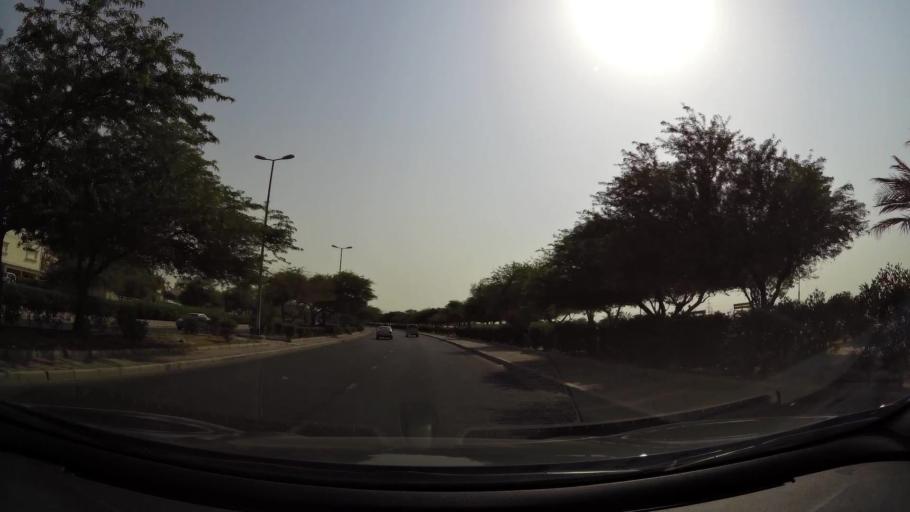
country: KW
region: Muhafazat al Jahra'
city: Al Jahra'
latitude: 29.3286
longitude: 47.6471
